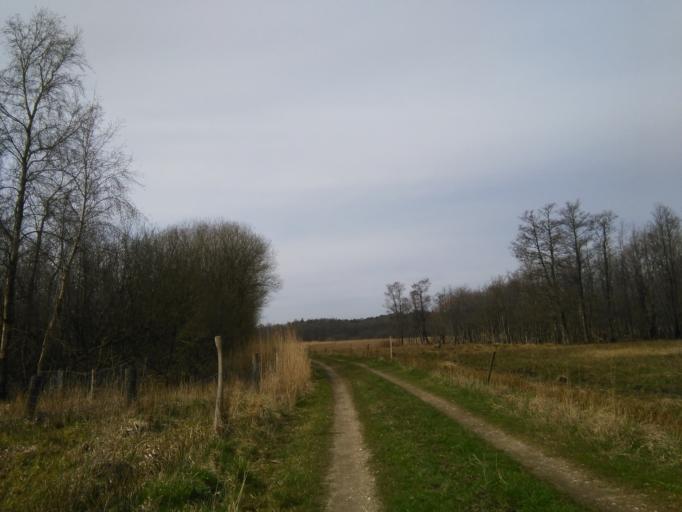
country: DK
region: Central Jutland
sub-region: Odder Kommune
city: Odder
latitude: 55.8855
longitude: 10.1152
